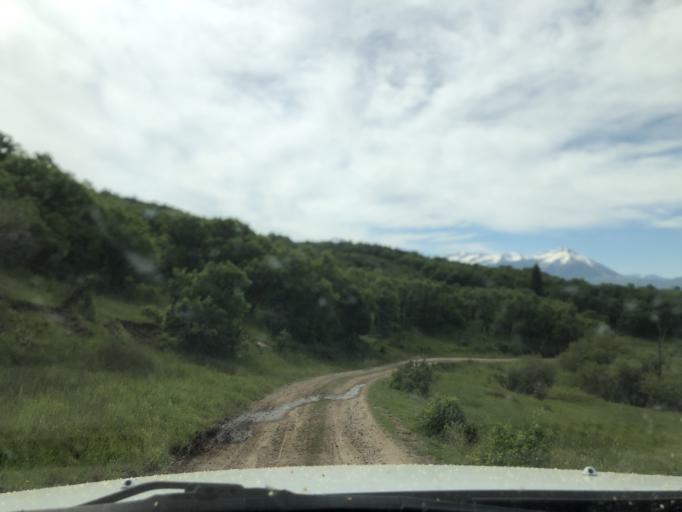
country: US
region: Colorado
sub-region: Delta County
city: Paonia
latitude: 39.0164
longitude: -107.3409
